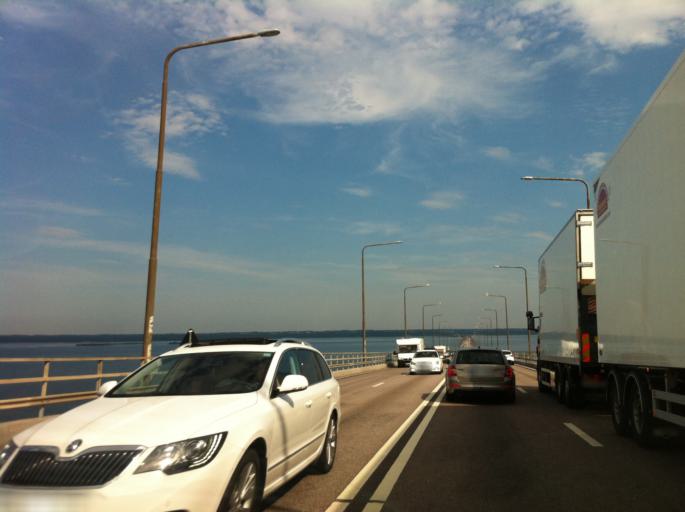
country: SE
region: Kalmar
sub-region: Kalmar Kommun
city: Kalmar
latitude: 56.6781
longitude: 16.3994
